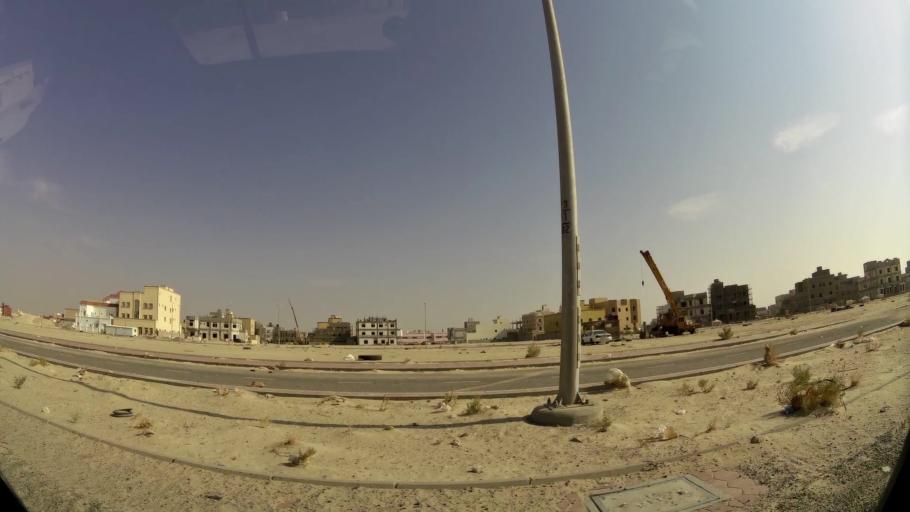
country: KW
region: Al Ahmadi
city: Al Wafrah
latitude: 28.7863
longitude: 48.0479
